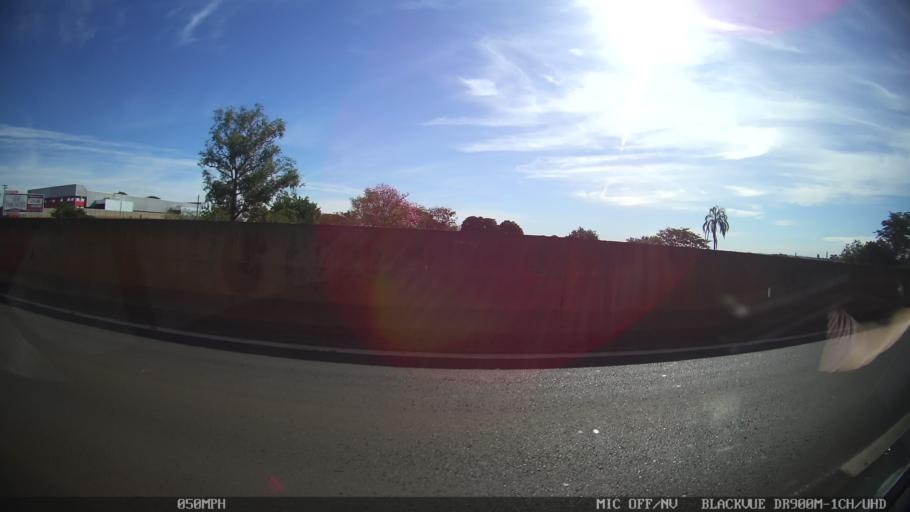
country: BR
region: Sao Paulo
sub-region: Sao Jose Do Rio Preto
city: Sao Jose do Rio Preto
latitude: -20.7420
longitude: -49.3379
